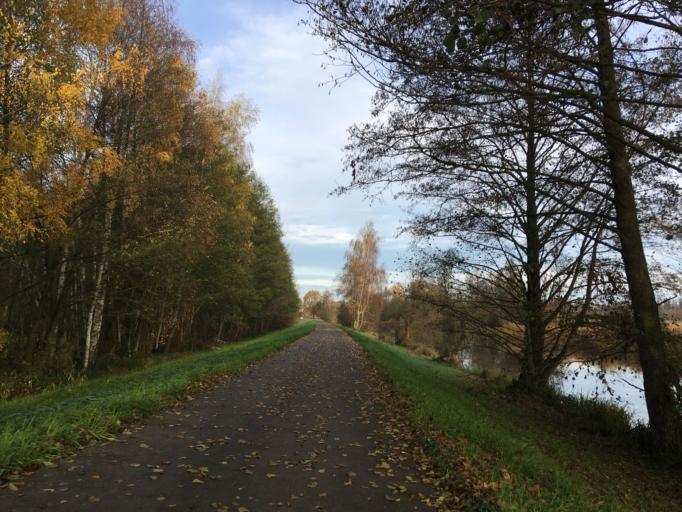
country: DE
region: Brandenburg
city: Luebben
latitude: 51.9168
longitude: 13.9175
